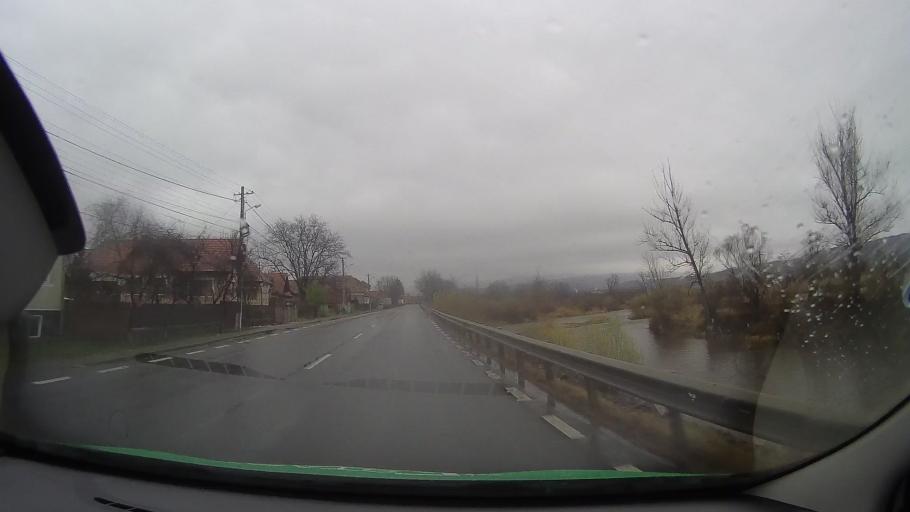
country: RO
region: Mures
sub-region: Comuna Brancovenesti
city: Valenii de Mures
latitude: 46.8865
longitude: 24.7905
